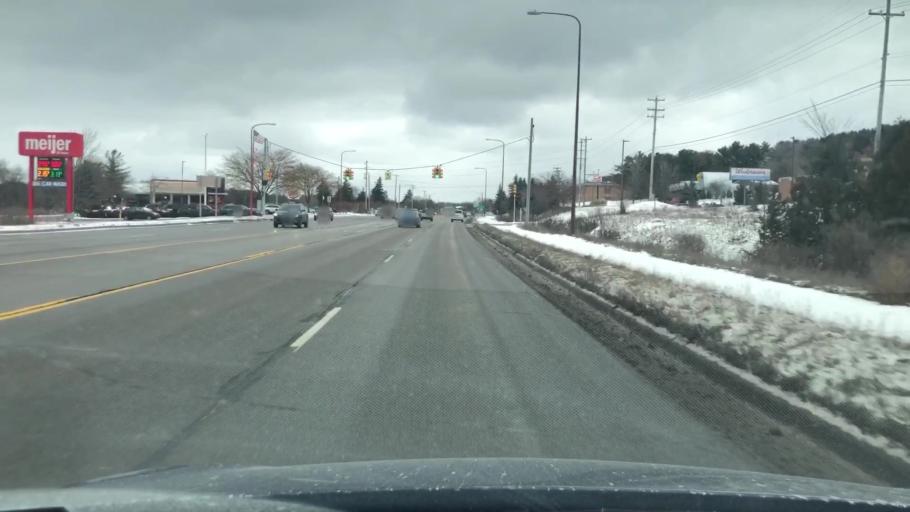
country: US
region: Michigan
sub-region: Grand Traverse County
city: Traverse City
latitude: 44.7428
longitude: -85.6416
